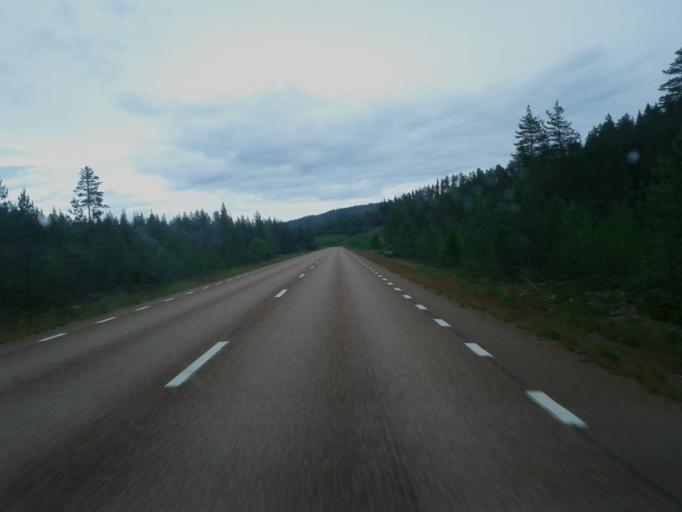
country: SE
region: Dalarna
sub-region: Alvdalens Kommun
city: AElvdalen
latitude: 61.2763
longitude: 13.8941
